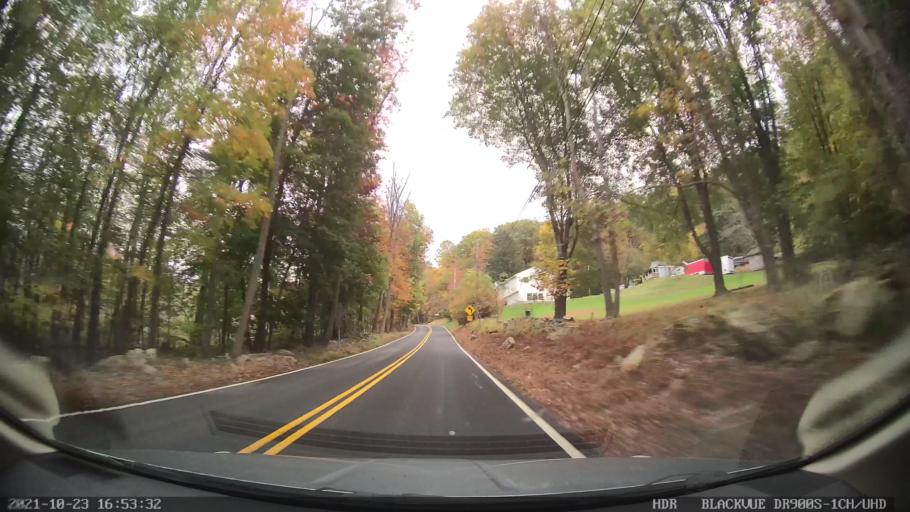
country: US
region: Pennsylvania
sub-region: Berks County
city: Red Lion
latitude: 40.4569
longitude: -75.5870
